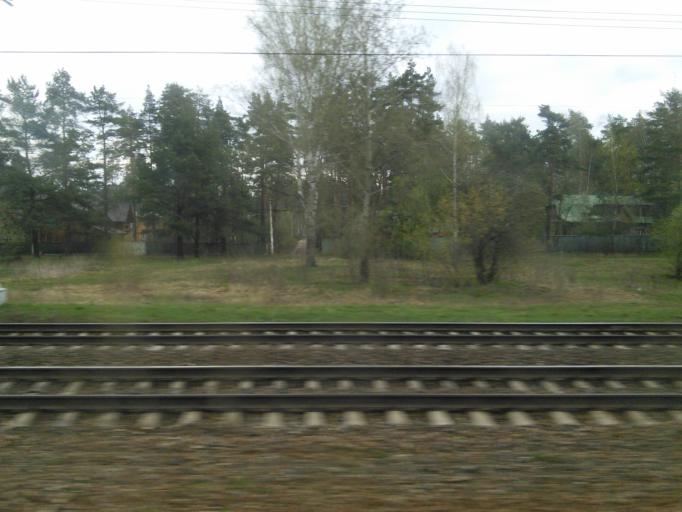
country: RU
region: Moskovskaya
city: Kratovo
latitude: 55.5851
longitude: 38.1774
